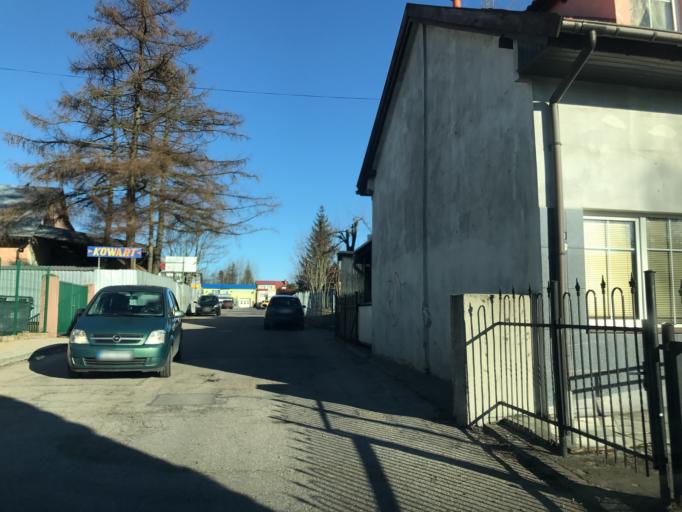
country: PL
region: Warmian-Masurian Voivodeship
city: Dobre Miasto
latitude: 53.9891
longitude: 20.3915
